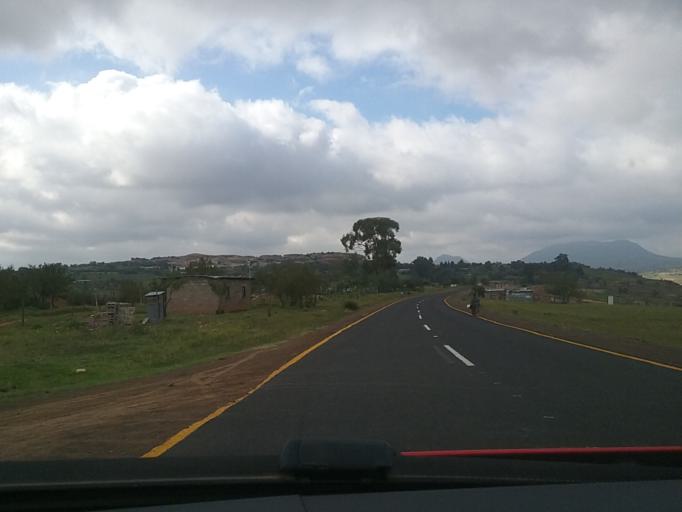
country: LS
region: Berea
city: Teyateyaneng
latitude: -29.1762
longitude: 27.7850
